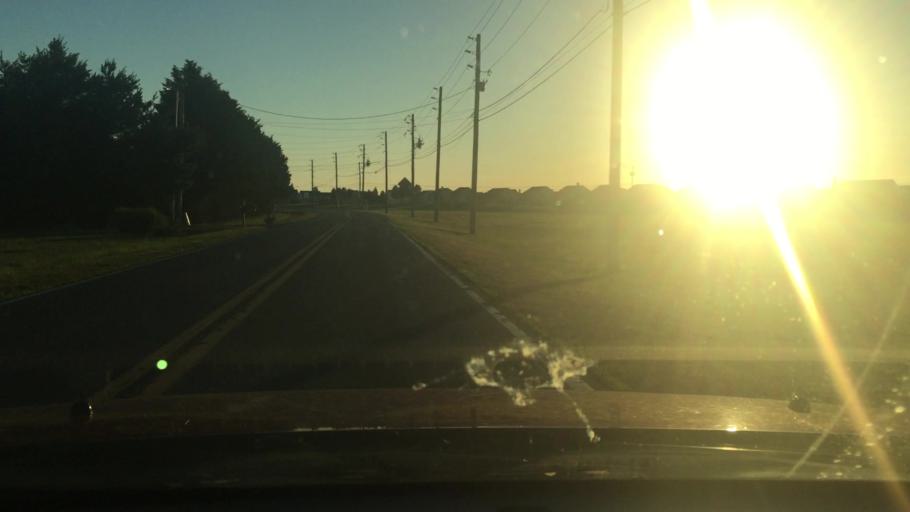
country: US
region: Delaware
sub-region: Kent County
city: Riverview
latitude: 39.0521
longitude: -75.5162
